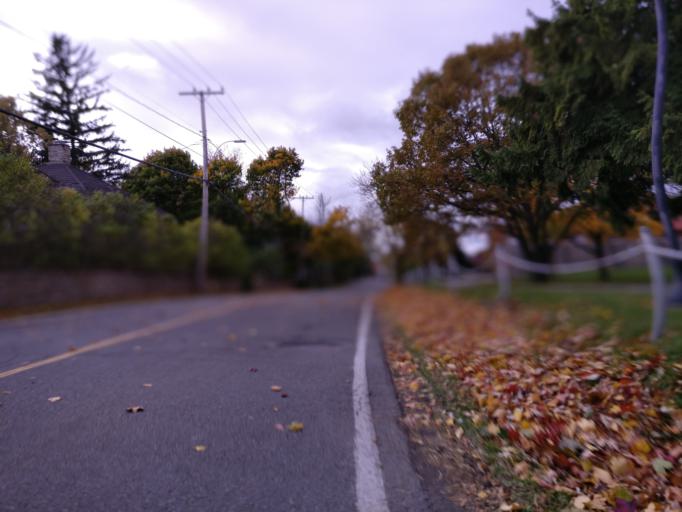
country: CA
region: Quebec
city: Sainte-Anne-de-Bellevue
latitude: 45.4047
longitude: -73.9372
